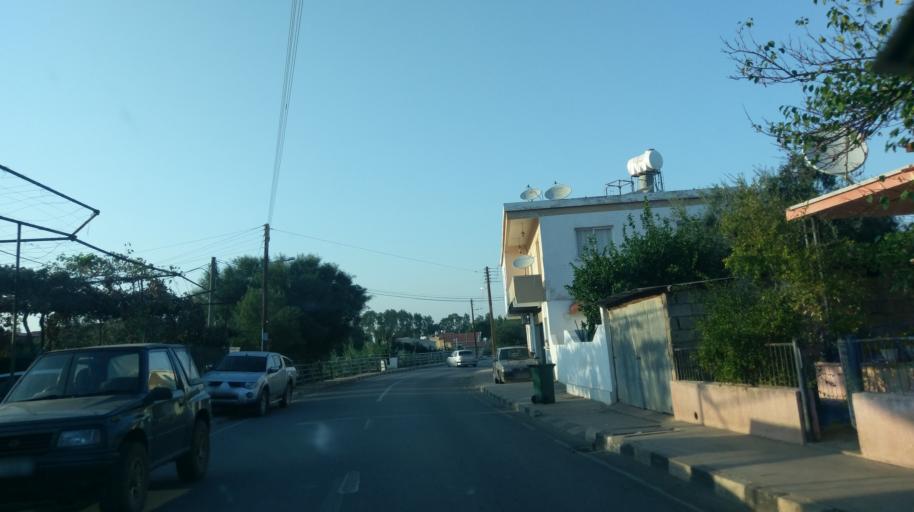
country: CY
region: Lefkosia
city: Astromeritis
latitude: 35.1629
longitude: 33.0143
